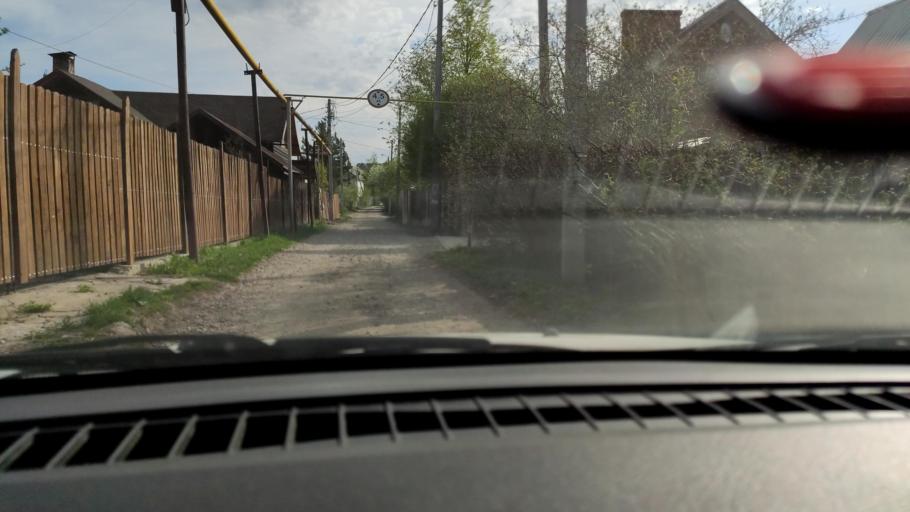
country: RU
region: Perm
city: Froly
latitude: 57.9458
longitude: 56.3012
